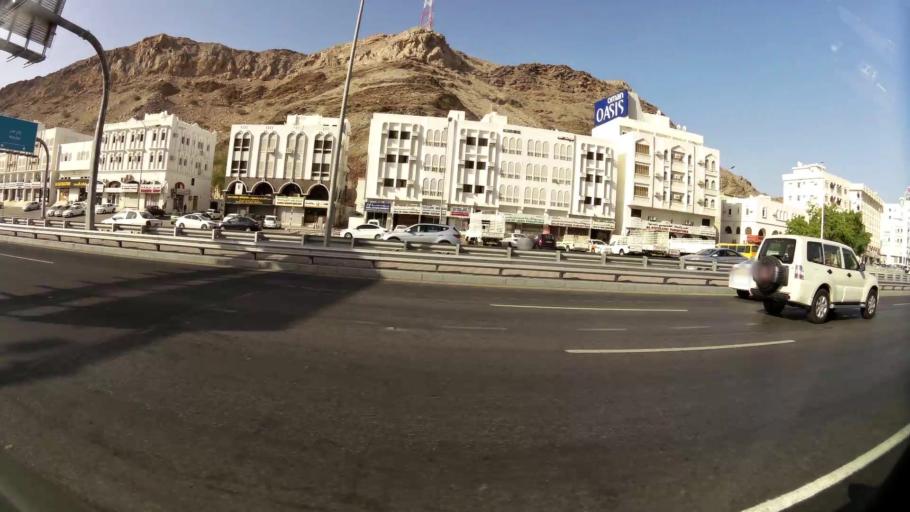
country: OM
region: Muhafazat Masqat
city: Muscat
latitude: 23.5892
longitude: 58.5327
